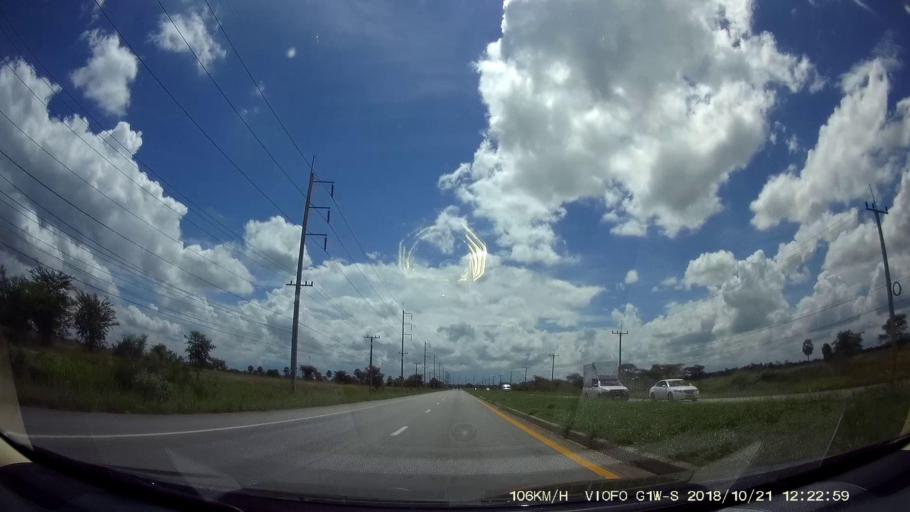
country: TH
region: Nakhon Ratchasima
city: Dan Khun Thot
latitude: 15.2529
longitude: 101.7890
